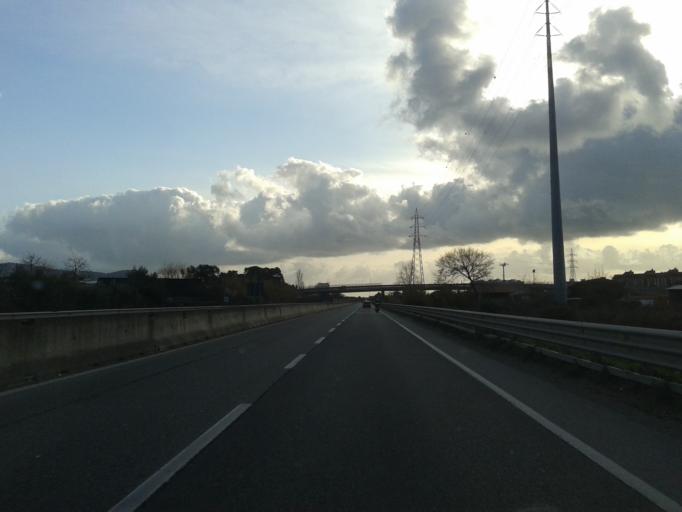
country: IT
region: Tuscany
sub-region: Provincia di Livorno
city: Livorno
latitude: 43.5305
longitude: 10.3331
